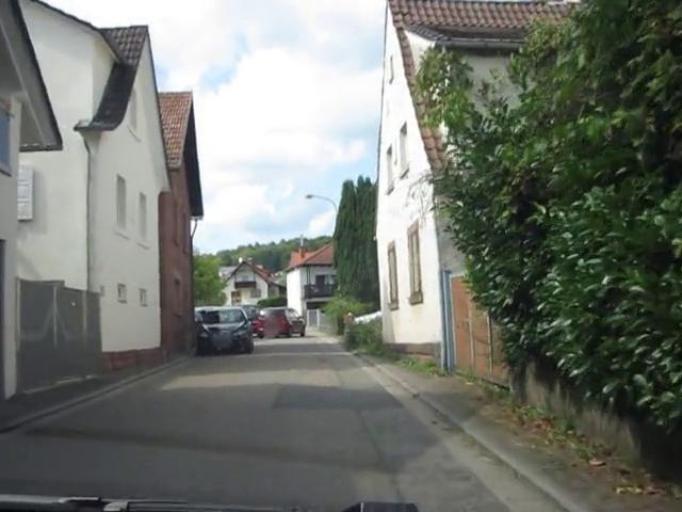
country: DE
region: Rheinland-Pfalz
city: Volkersweiler
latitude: 49.1635
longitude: 7.9252
